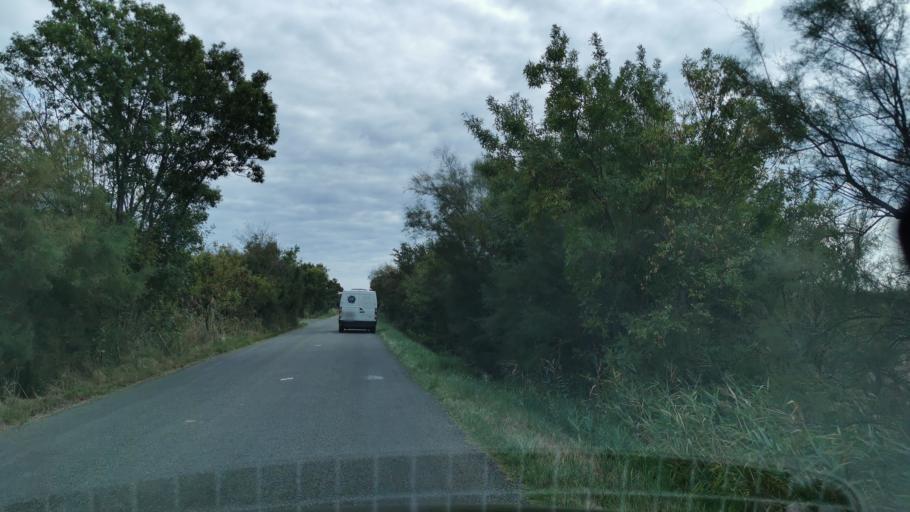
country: FR
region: Languedoc-Roussillon
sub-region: Departement de l'Herault
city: Vendres
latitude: 43.2322
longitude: 3.1966
